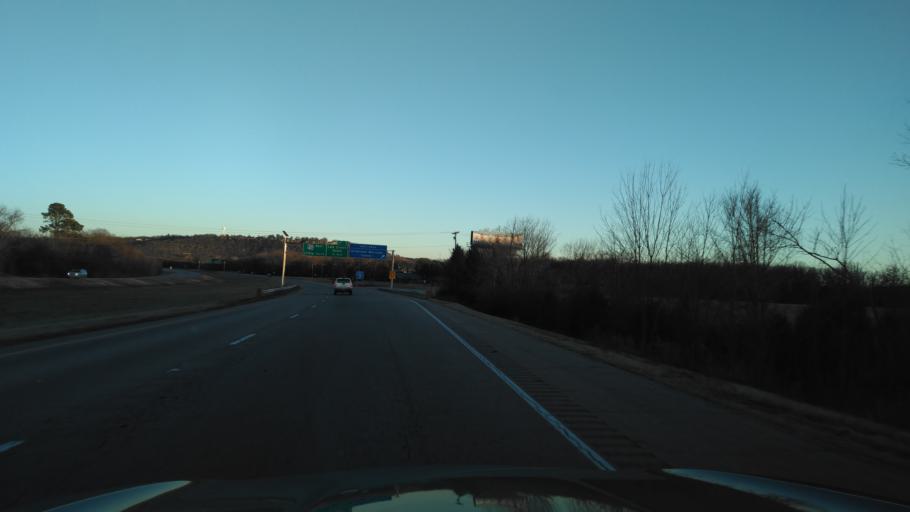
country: US
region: Arkansas
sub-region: Crawford County
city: Van Buren
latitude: 35.4604
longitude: -94.4024
